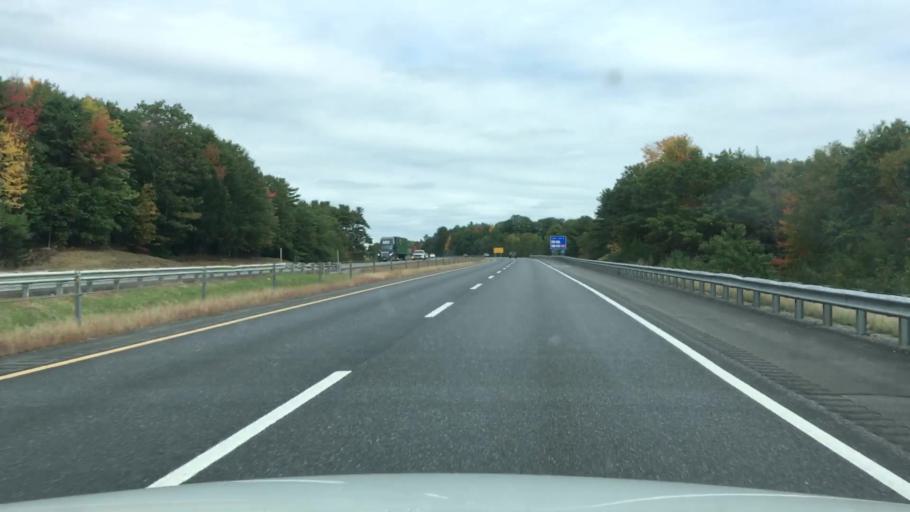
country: US
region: Maine
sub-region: Kennebec County
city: Gardiner
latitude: 44.1935
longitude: -69.8273
